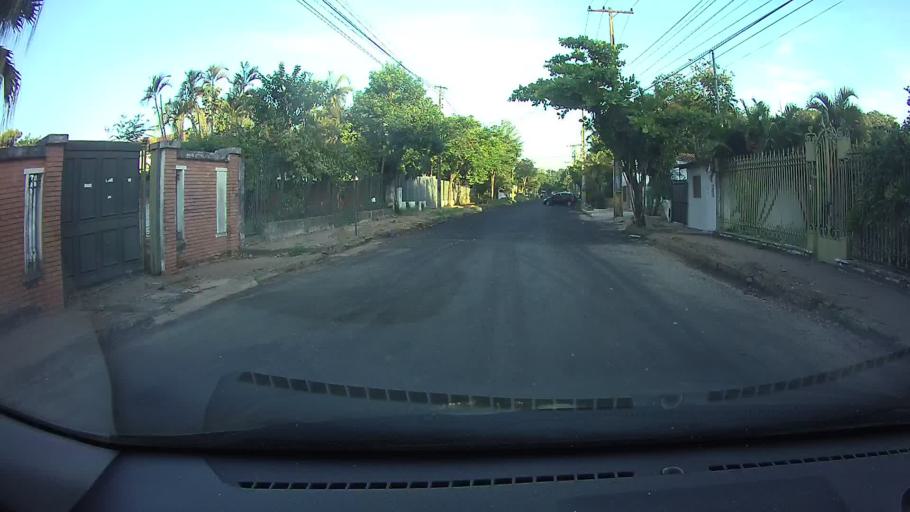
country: PY
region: Central
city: Fernando de la Mora
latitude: -25.2623
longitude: -57.5145
